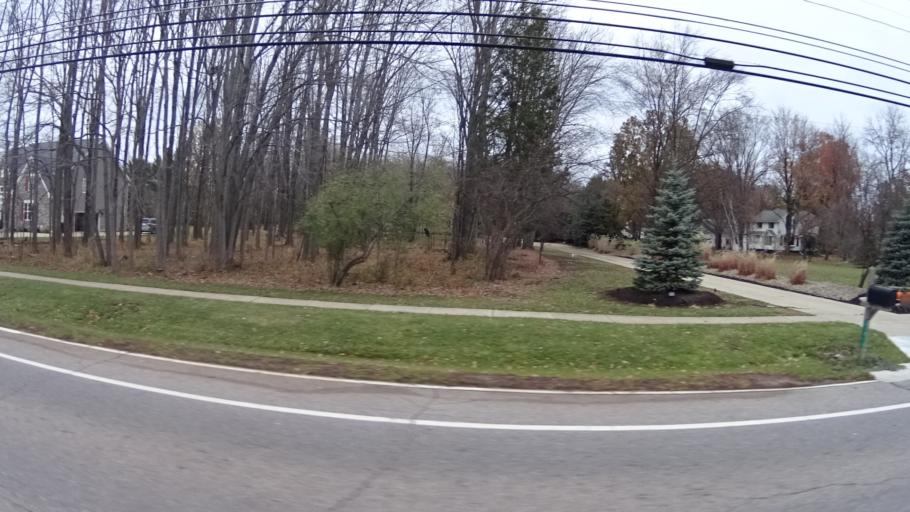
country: US
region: Ohio
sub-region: Lorain County
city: Avon Lake
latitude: 41.4928
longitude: -81.9823
